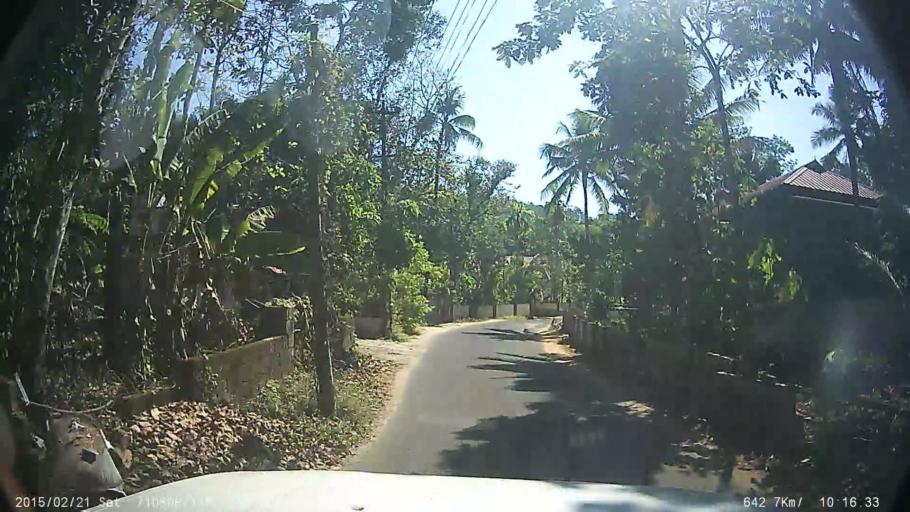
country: IN
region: Kerala
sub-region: Ernakulam
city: Muvattupuzha
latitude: 9.8811
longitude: 76.6451
